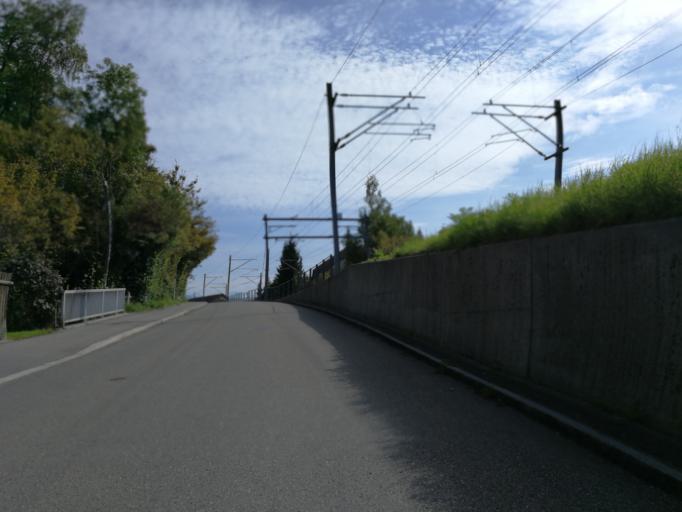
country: CH
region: Zurich
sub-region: Bezirk Meilen
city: Obermeilen
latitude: 47.2645
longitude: 8.6647
